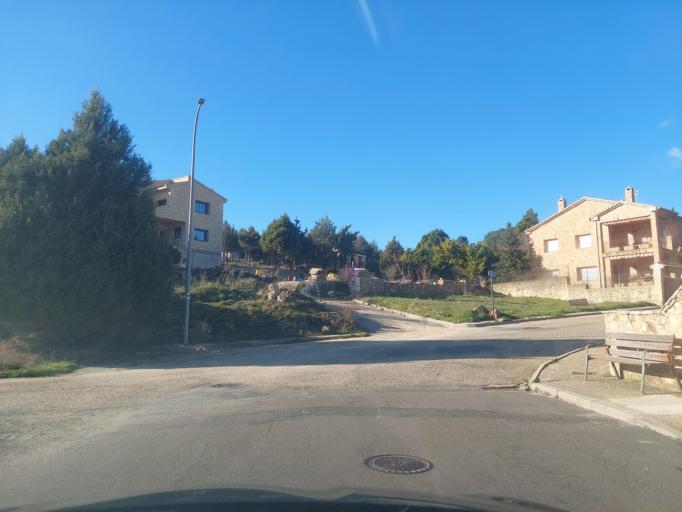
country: ES
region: Castille and Leon
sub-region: Provincia de Segovia
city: Pradena
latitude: 41.1325
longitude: -3.6903
